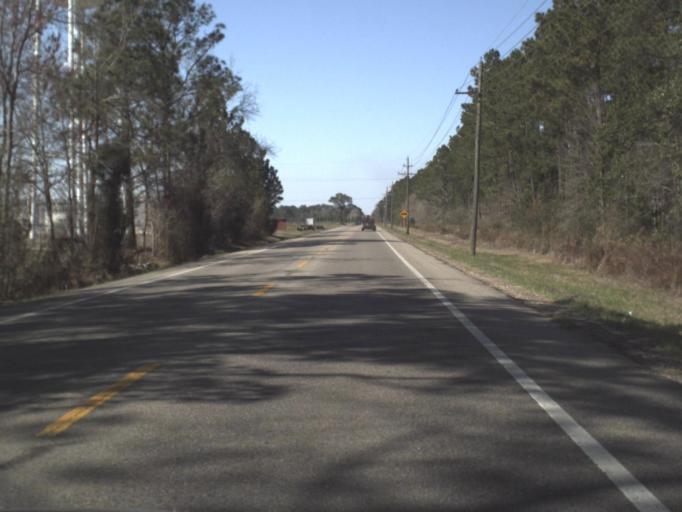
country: US
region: Florida
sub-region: Calhoun County
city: Blountstown
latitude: 30.4869
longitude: -85.1072
